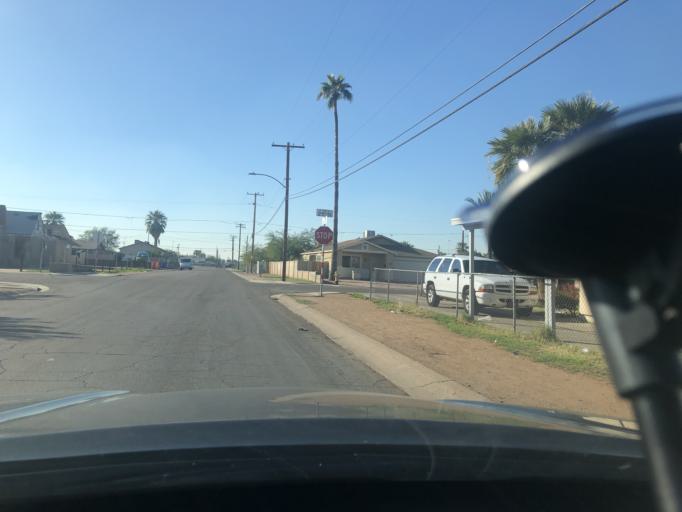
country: US
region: Arizona
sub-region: Maricopa County
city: Phoenix
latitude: 33.4604
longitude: -112.0277
